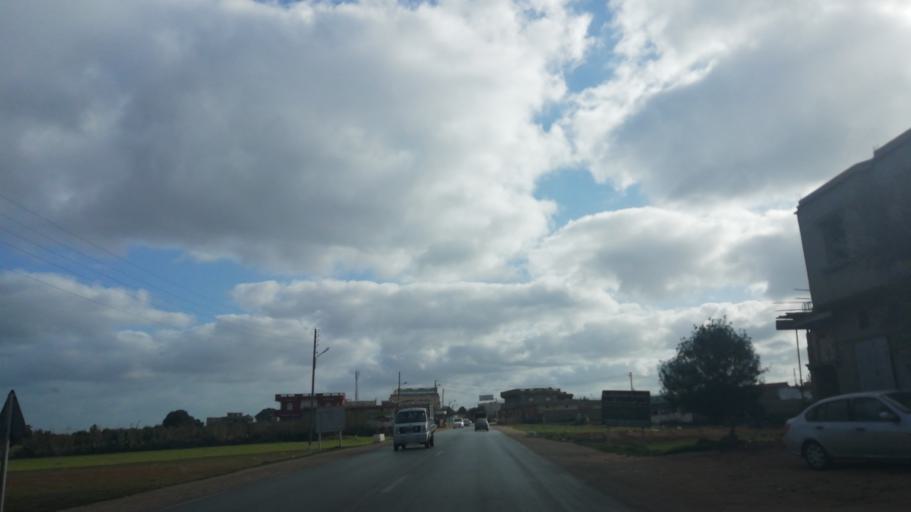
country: DZ
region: Relizane
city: Mazouna
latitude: 36.2607
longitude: 0.6101
